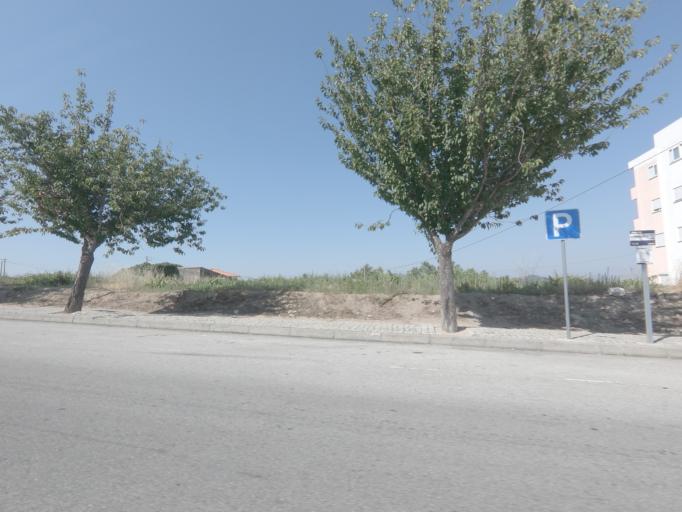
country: PT
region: Viseu
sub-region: Moimenta da Beira
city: Moimenta da Beira
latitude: 40.9788
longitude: -7.6163
